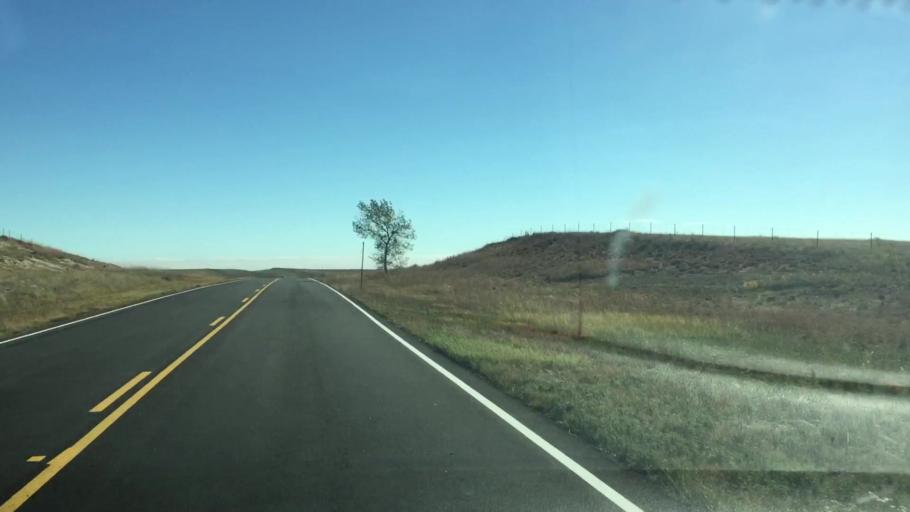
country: US
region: Colorado
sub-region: Lincoln County
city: Limon
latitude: 39.2955
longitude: -103.8708
